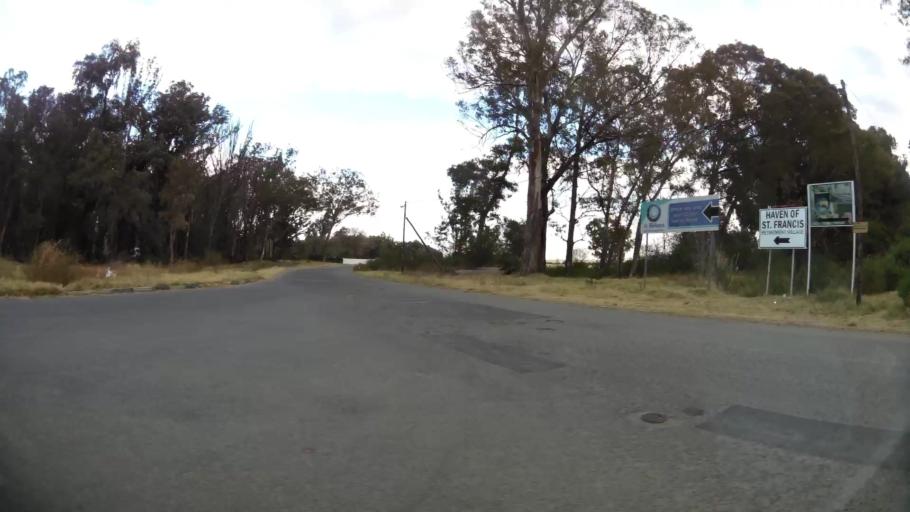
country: ZA
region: Orange Free State
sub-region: Lejweleputswa District Municipality
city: Welkom
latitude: -27.9973
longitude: 26.7106
